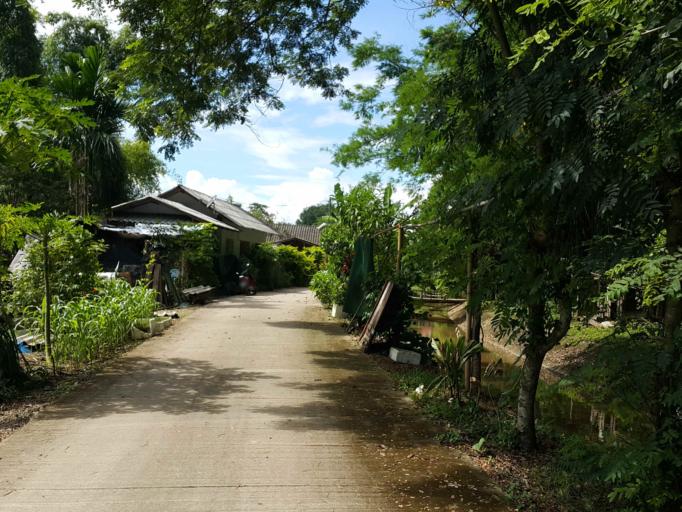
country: TH
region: Chiang Mai
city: Mae Taeng
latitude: 18.9598
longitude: 98.9165
